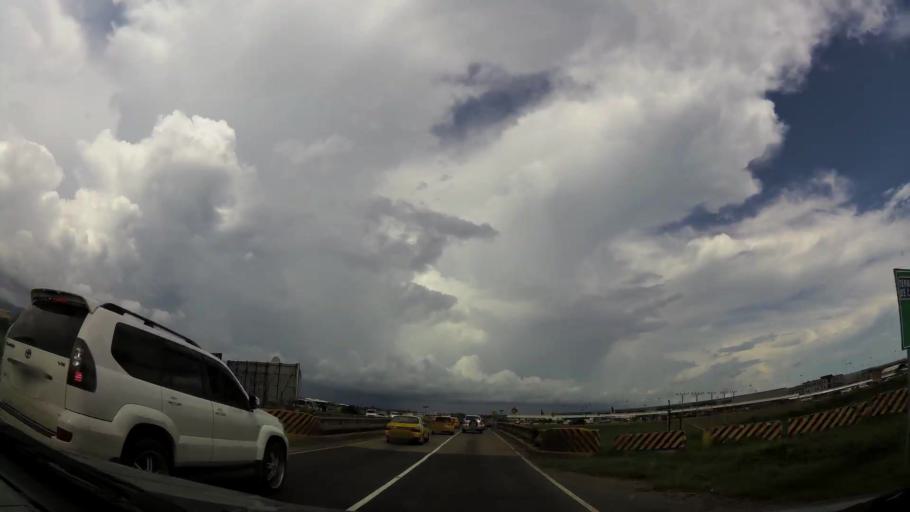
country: PA
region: Panama
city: Tocumen
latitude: 9.0705
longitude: -79.3895
